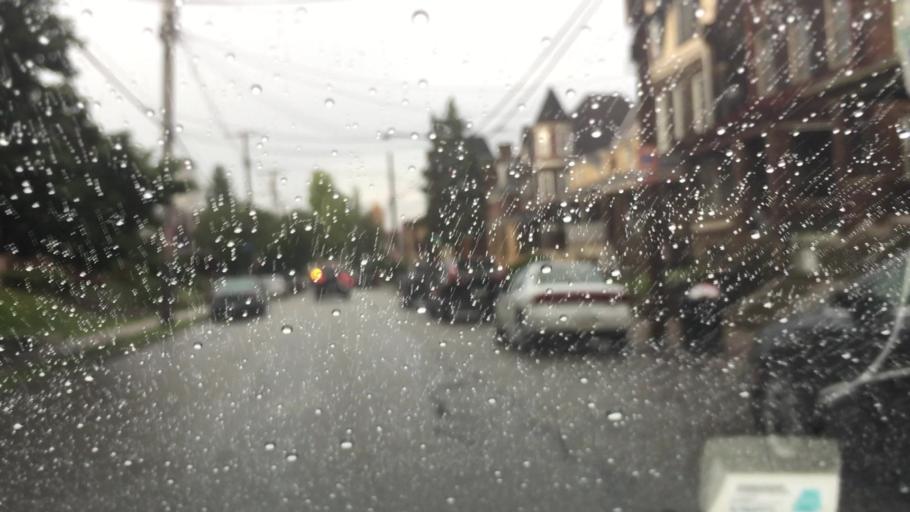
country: US
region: Pennsylvania
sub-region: Allegheny County
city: Bloomfield
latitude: 40.4323
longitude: -79.9537
